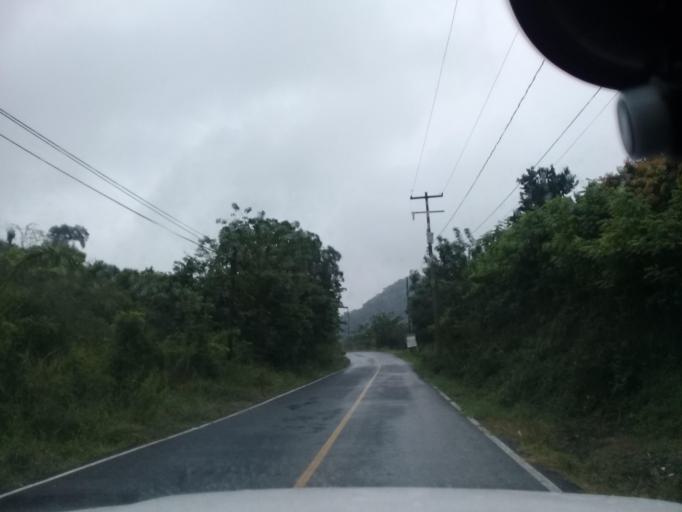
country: MX
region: Veracruz
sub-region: Chalma
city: San Pedro Coyutla
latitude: 21.2310
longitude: -98.4537
